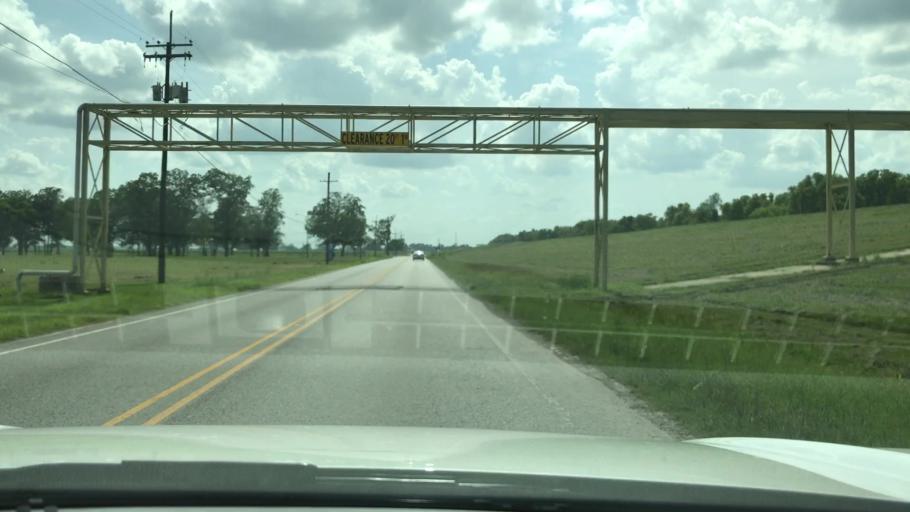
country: US
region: Louisiana
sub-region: Iberville Parish
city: Plaquemine
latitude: 30.2731
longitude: -91.1828
